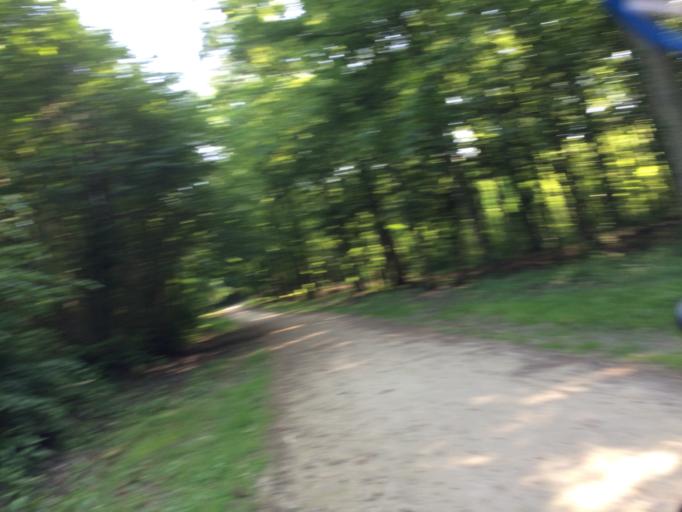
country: FR
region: Ile-de-France
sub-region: Departement de l'Essonne
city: Fleury-Merogis
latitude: 48.6330
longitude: 2.3540
